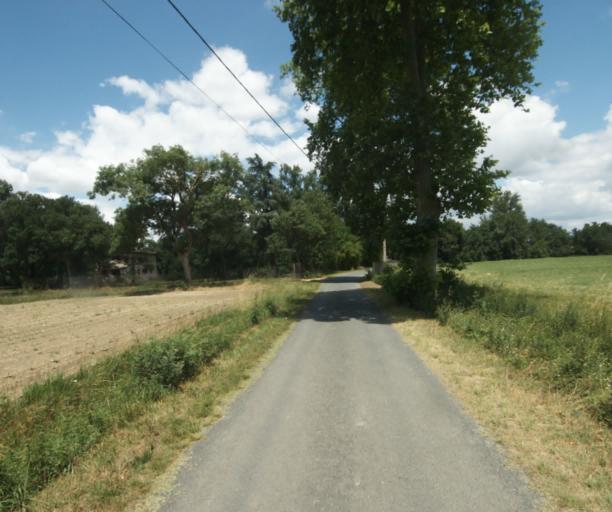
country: FR
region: Midi-Pyrenees
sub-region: Departement du Tarn
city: Puylaurens
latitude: 43.5191
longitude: 2.0217
